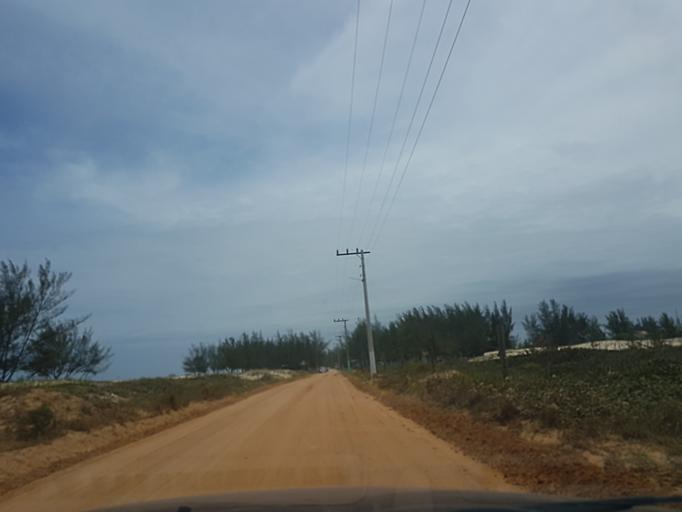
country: BR
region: Santa Catarina
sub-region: Jaguaruna
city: Jaguaruna
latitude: -28.6701
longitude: -48.9736
